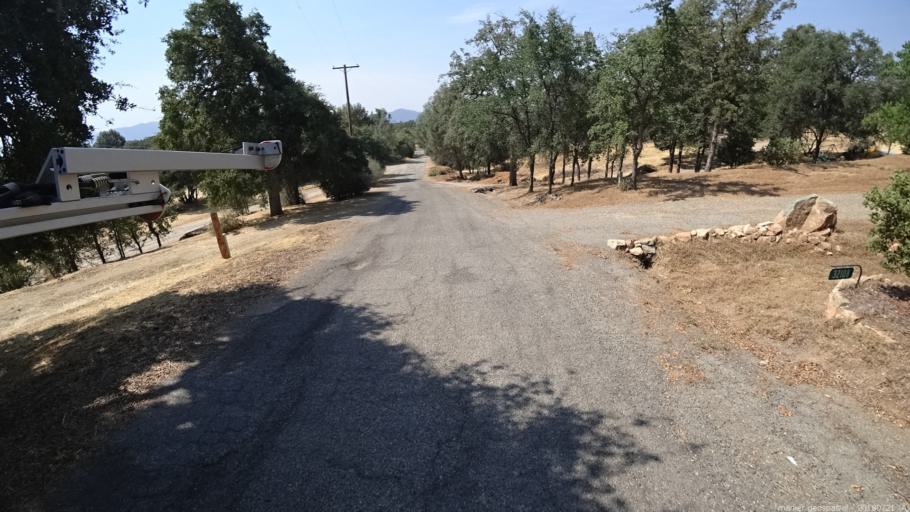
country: US
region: California
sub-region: Fresno County
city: Auberry
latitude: 37.2142
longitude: -119.5214
